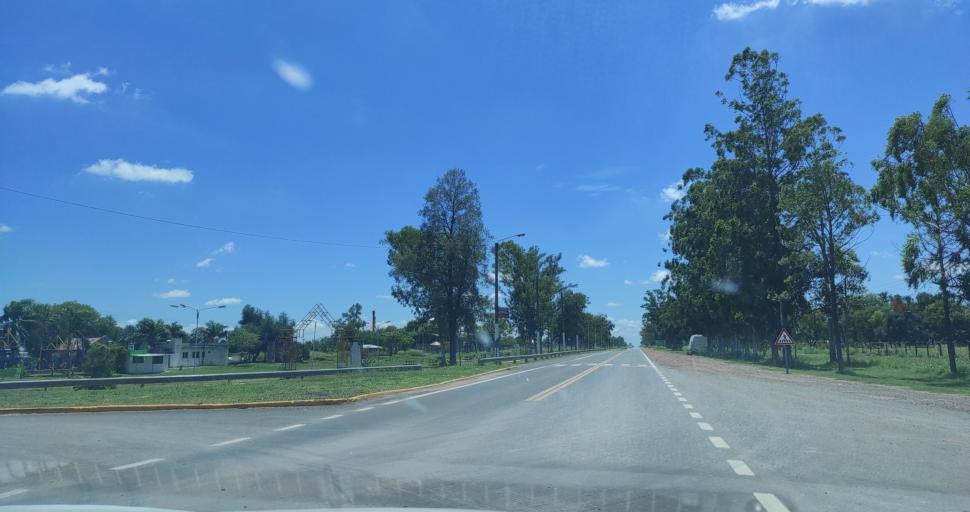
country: AR
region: Chaco
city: Las Brenas
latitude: -27.0992
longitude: -61.0663
